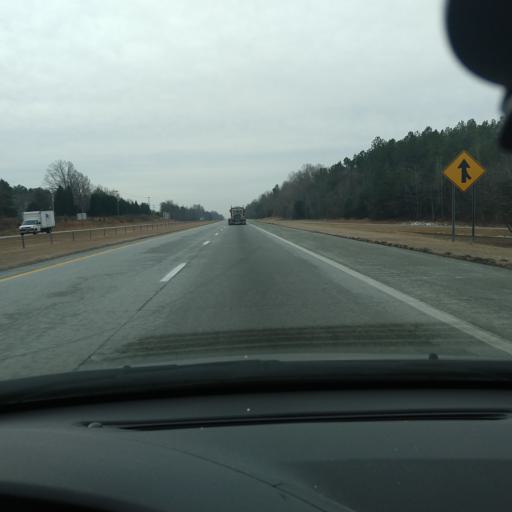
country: US
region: North Carolina
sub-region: Davidson County
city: Lexington
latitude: 35.8345
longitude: -80.2830
